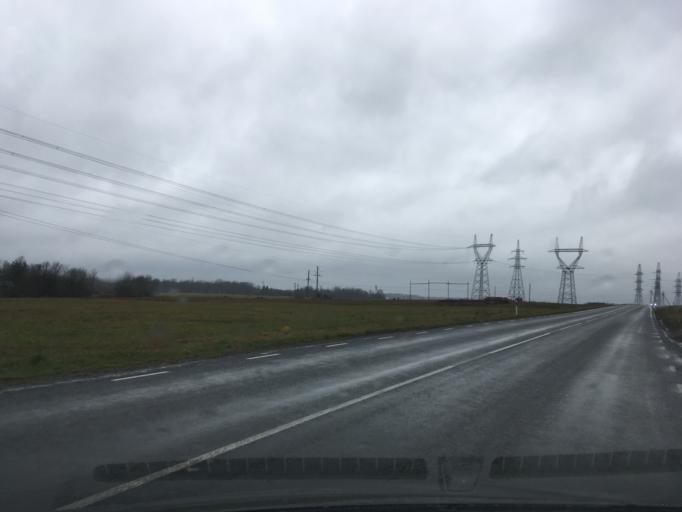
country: EE
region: Laeaene
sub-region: Lihula vald
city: Lihula
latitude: 58.6751
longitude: 23.8199
